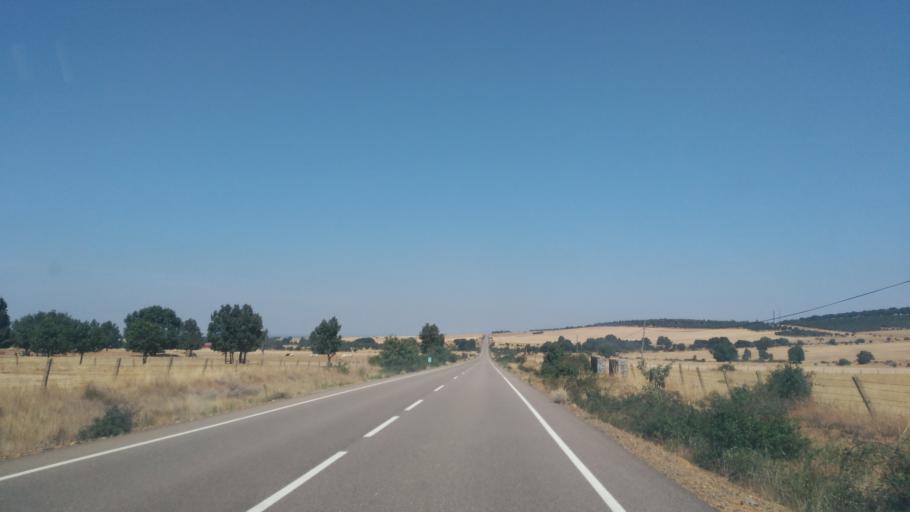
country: ES
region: Castille and Leon
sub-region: Provincia de Salamanca
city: Tamames
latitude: 40.6372
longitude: -6.1109
